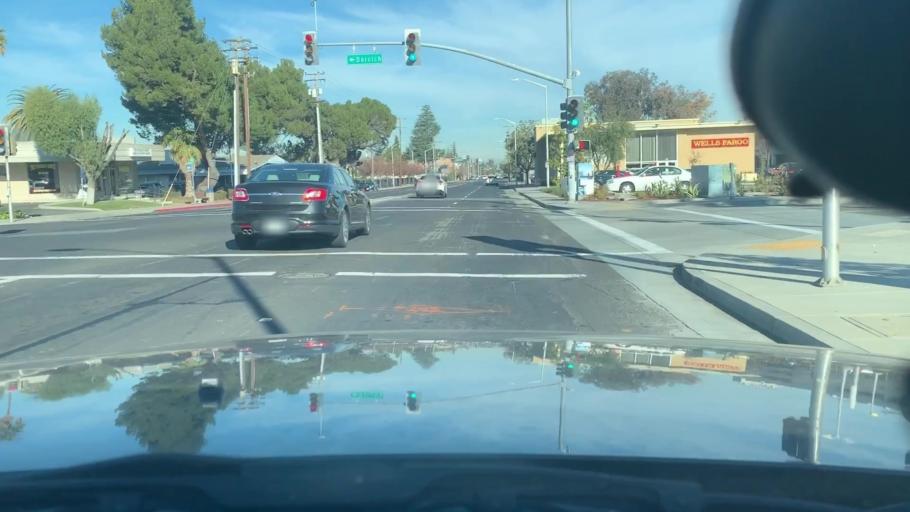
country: US
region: California
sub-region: Santa Clara County
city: Burbank
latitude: 37.3248
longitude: -121.9501
